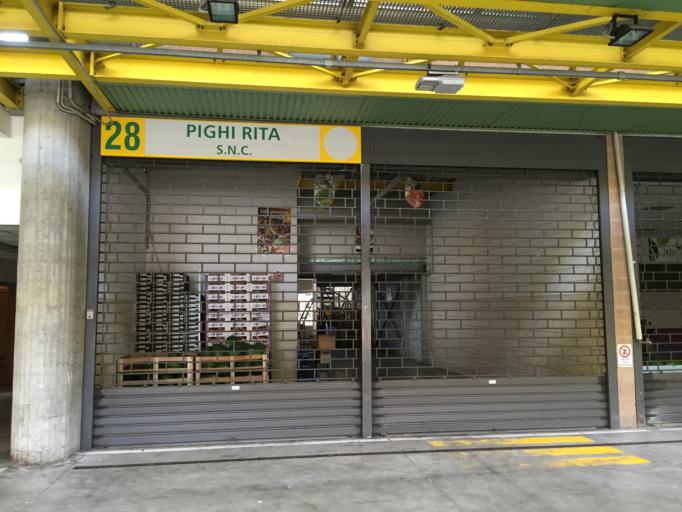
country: IT
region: Veneto
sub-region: Provincia di Verona
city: Dossobuono
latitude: 45.4115
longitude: 10.9208
